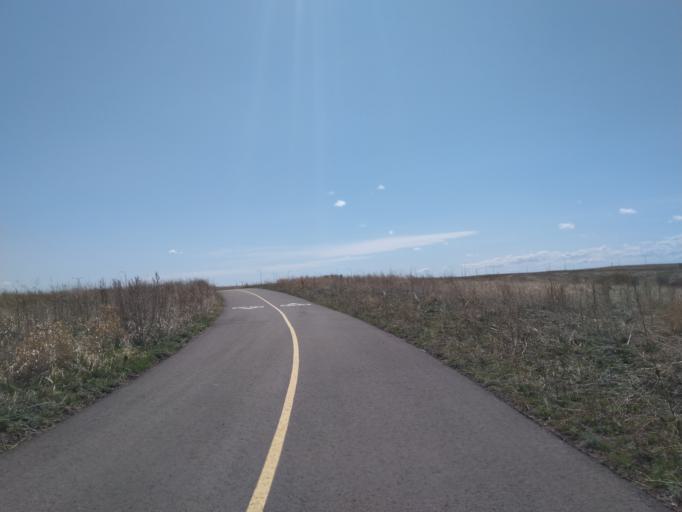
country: CA
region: Alberta
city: Chestermere
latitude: 51.0210
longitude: -113.9245
